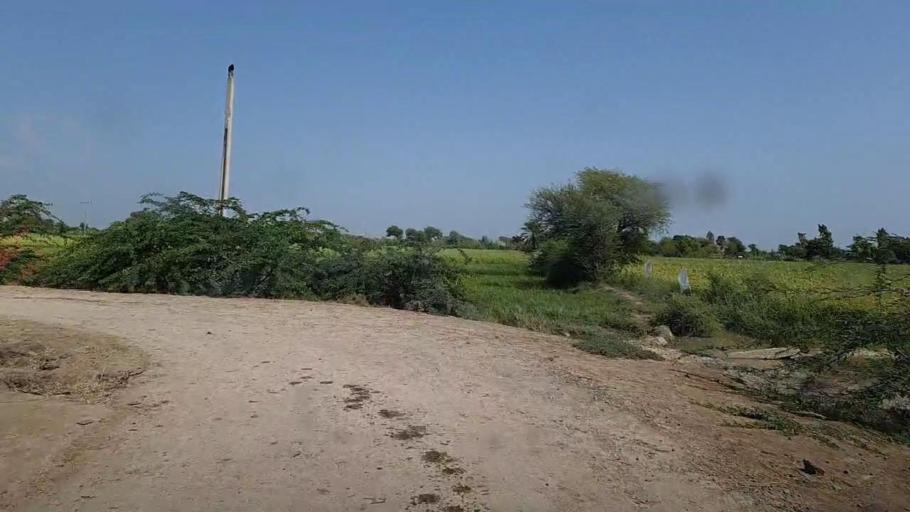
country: PK
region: Sindh
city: Mirpur Batoro
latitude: 24.6447
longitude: 68.4520
